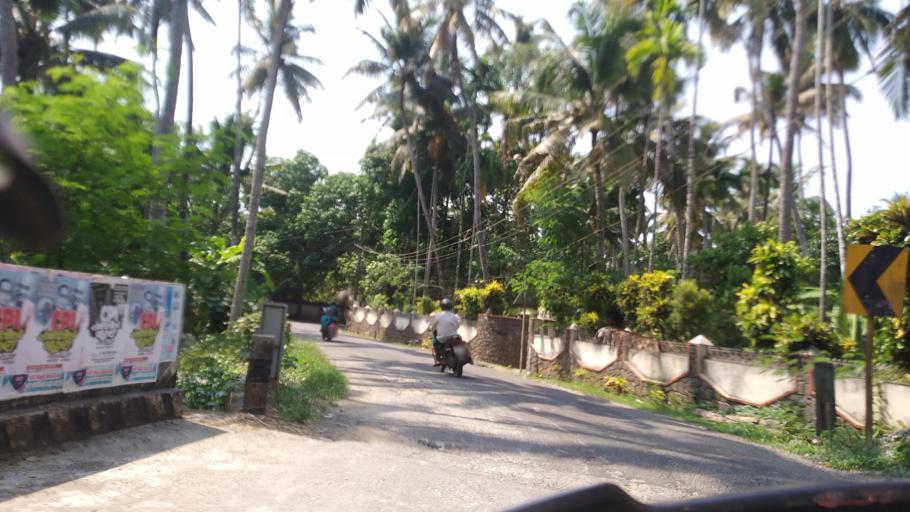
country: IN
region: Kerala
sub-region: Thrissur District
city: Irinjalakuda
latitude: 10.3006
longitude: 76.1316
